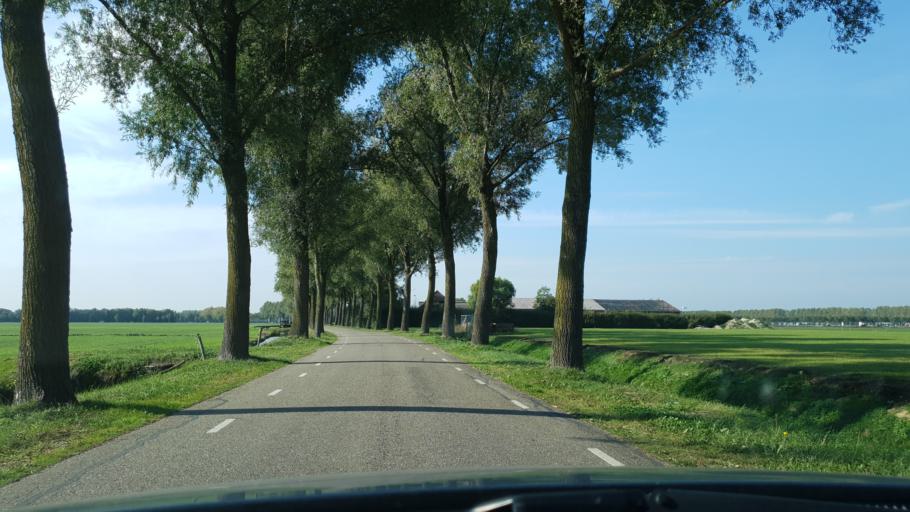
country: NL
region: Gelderland
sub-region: Gemeente Beuningen
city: Beuningen
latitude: 51.8381
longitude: 5.7487
